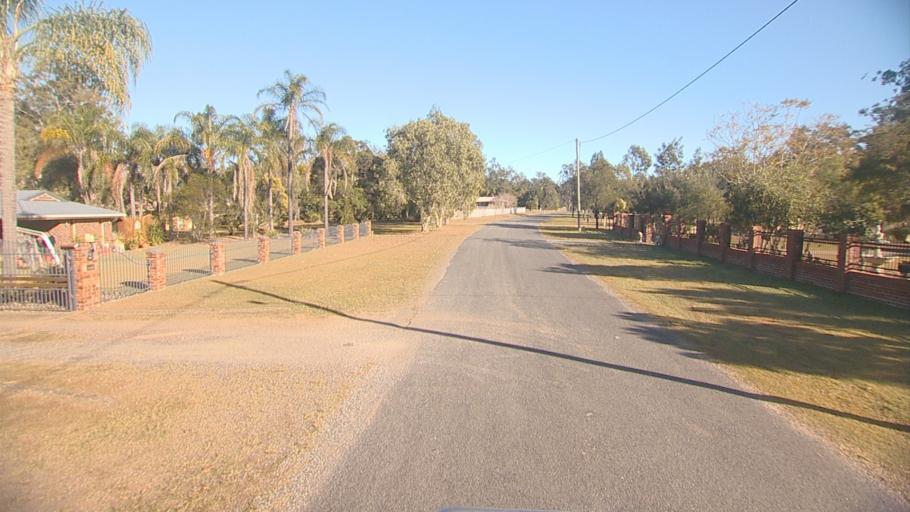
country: AU
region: Queensland
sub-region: Logan
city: North Maclean
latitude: -27.7448
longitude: 153.0114
